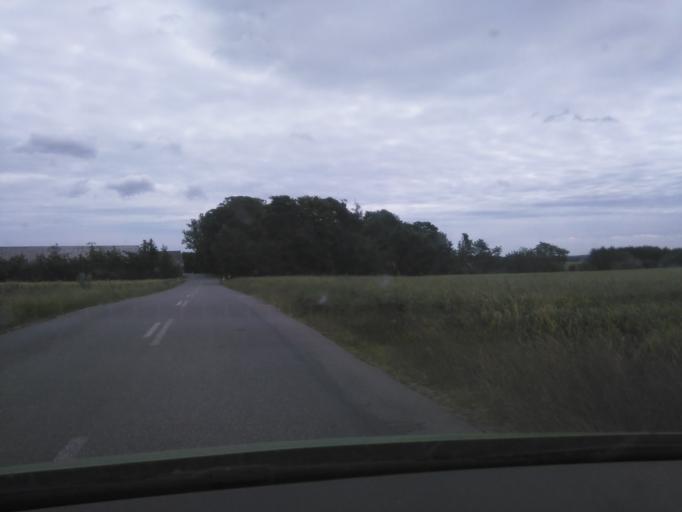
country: DK
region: Central Jutland
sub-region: Odder Kommune
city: Odder
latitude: 55.9960
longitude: 10.1158
